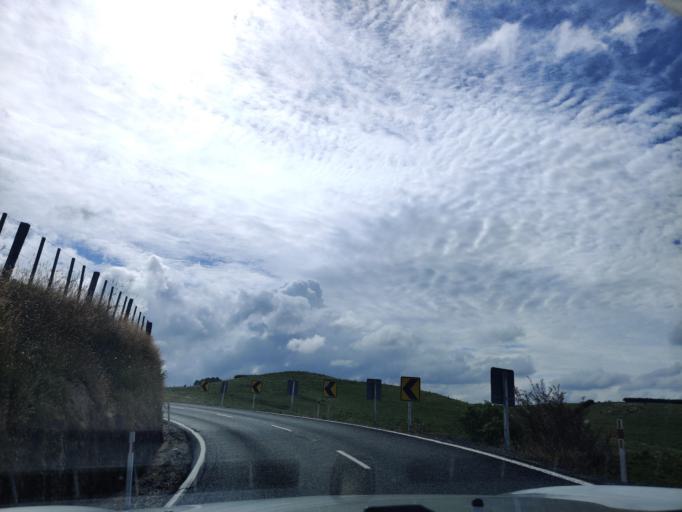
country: NZ
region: Waikato
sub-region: Otorohanga District
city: Otorohanga
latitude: -38.0916
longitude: 175.1521
